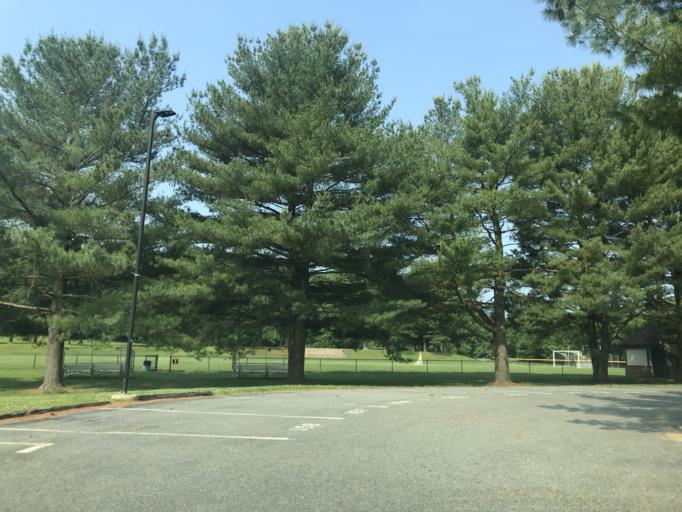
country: US
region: Maryland
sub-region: Harford County
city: South Bel Air
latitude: 39.5360
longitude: -76.3340
